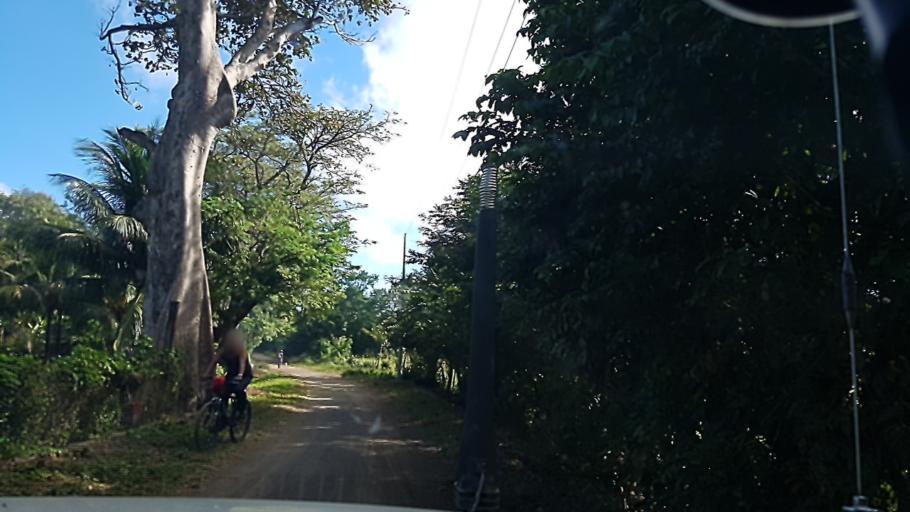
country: NI
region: Carazo
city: La Paz de Oriente
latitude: 11.8235
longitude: -86.1396
